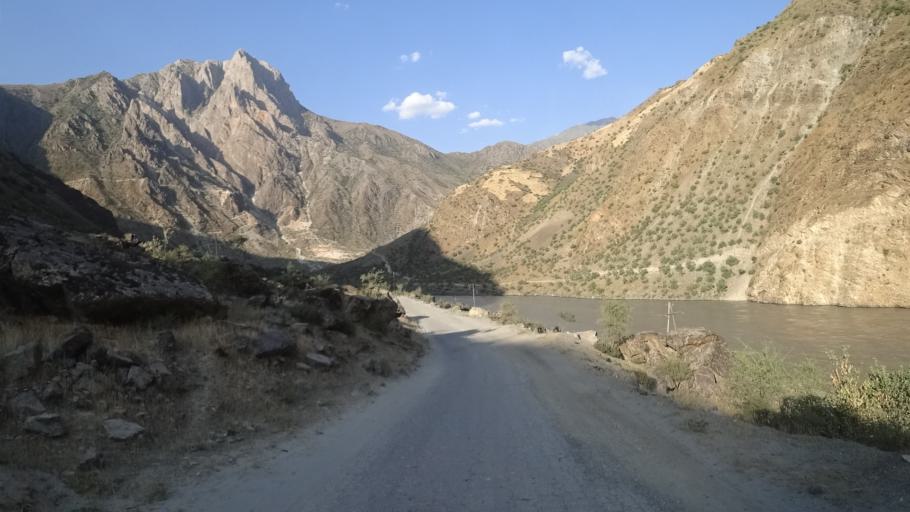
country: AF
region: Badakhshan
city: Maymay
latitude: 38.4815
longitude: 70.9783
